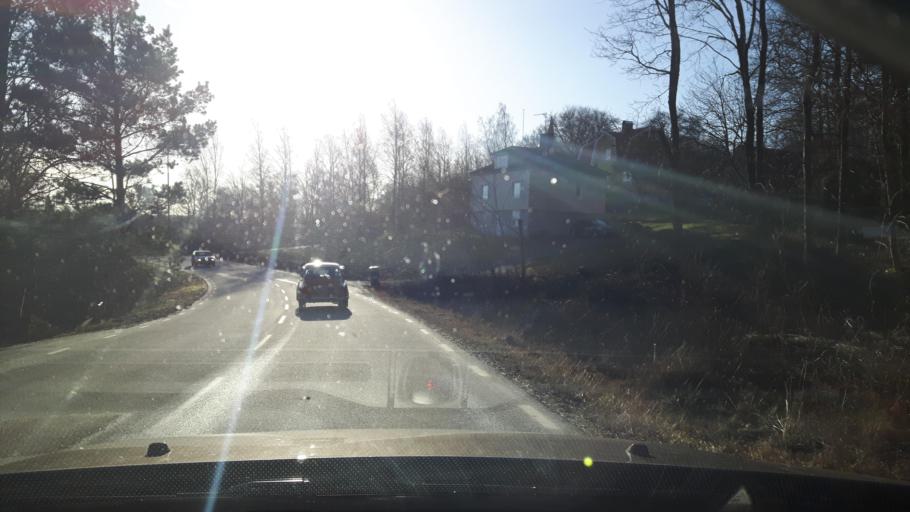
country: SE
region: Vaestra Goetaland
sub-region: Munkedals Kommun
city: Munkedal
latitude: 58.4884
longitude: 11.6938
